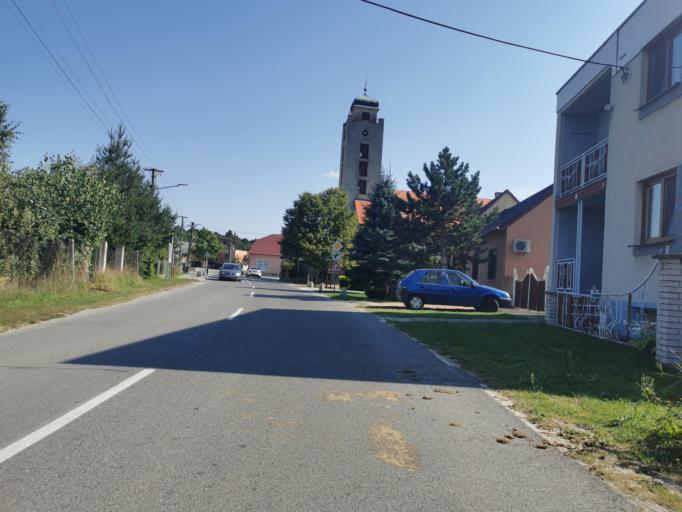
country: SK
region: Trnavsky
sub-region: Okres Senica
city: Senica
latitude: 48.6533
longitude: 17.2690
